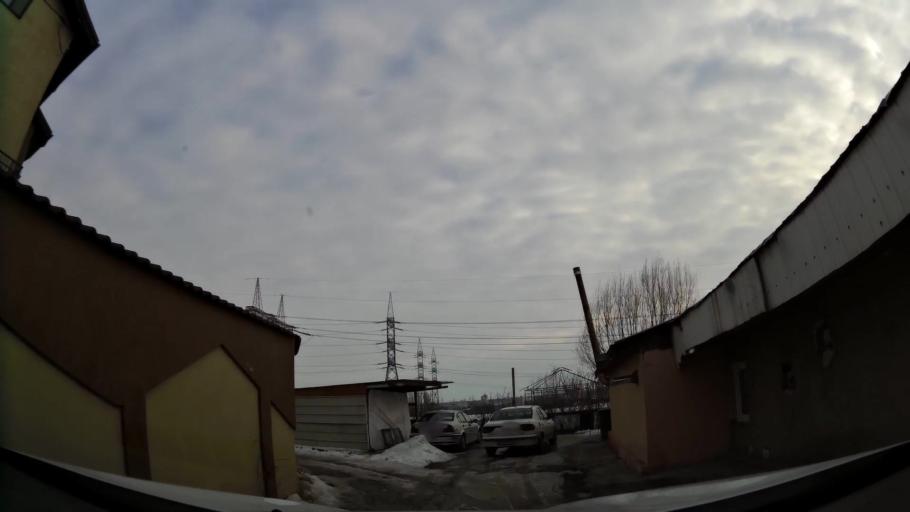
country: RO
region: Ilfov
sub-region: Comuna Glina
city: Catelu
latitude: 44.3990
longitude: 26.2158
